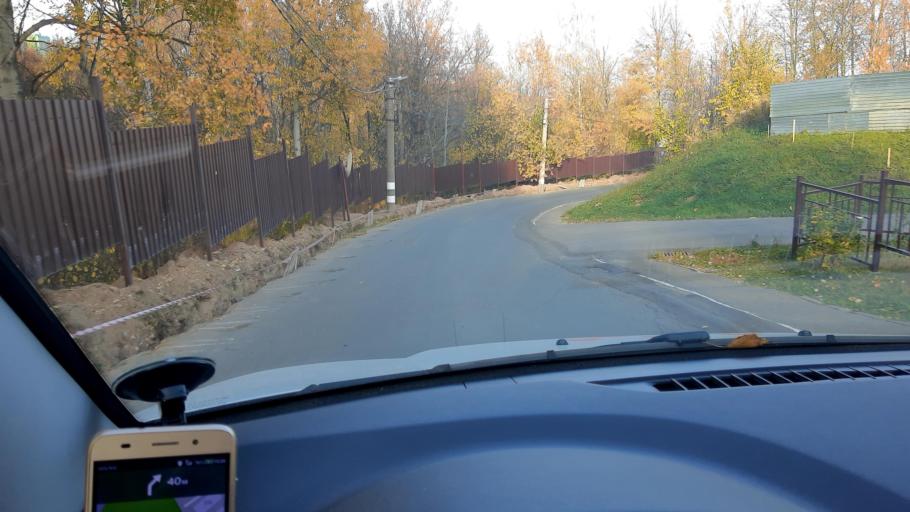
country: RU
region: Nizjnij Novgorod
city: Afonino
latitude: 56.2896
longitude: 44.0809
